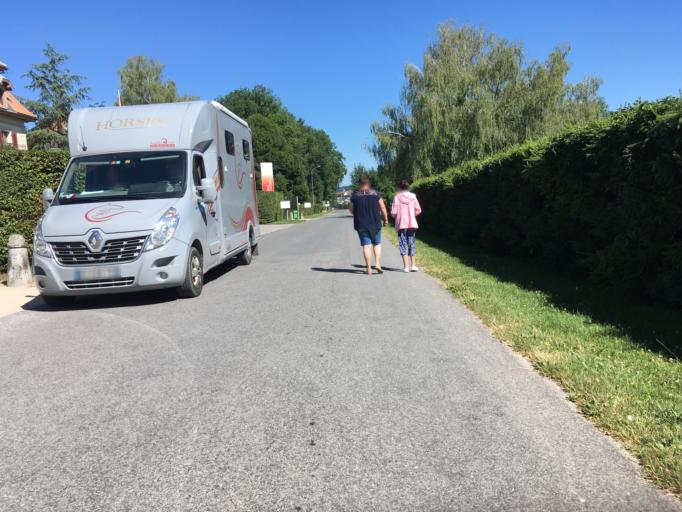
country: CH
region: Fribourg
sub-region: Broye District
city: Domdidier
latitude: 46.8866
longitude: 7.0170
